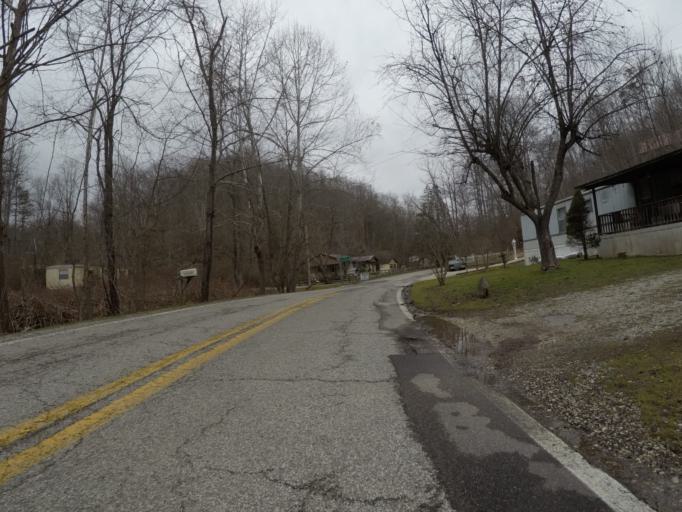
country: US
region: West Virginia
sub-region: Cabell County
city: Barboursville
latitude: 38.4475
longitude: -82.2561
